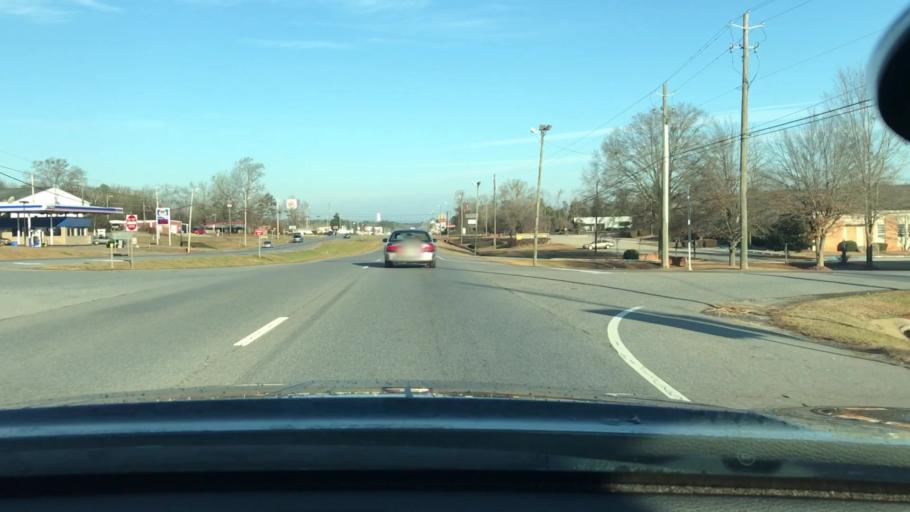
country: US
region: Alabama
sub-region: Talladega County
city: Childersburg
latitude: 33.2593
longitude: -86.3468
